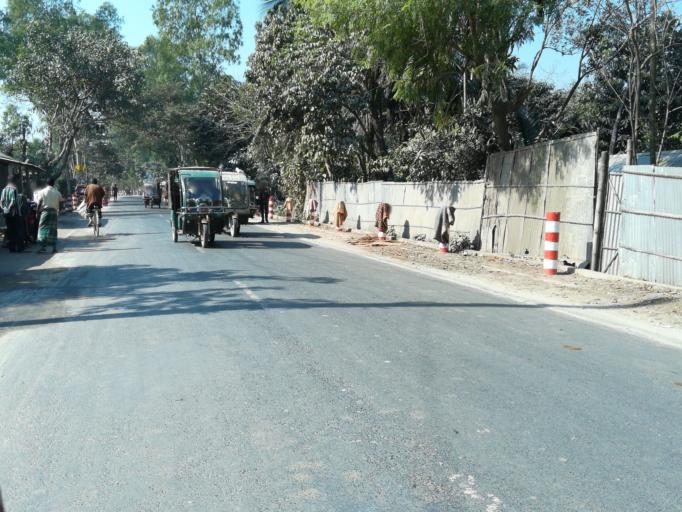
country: BD
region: Rangpur Division
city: Nageswari
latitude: 25.8180
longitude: 89.6638
